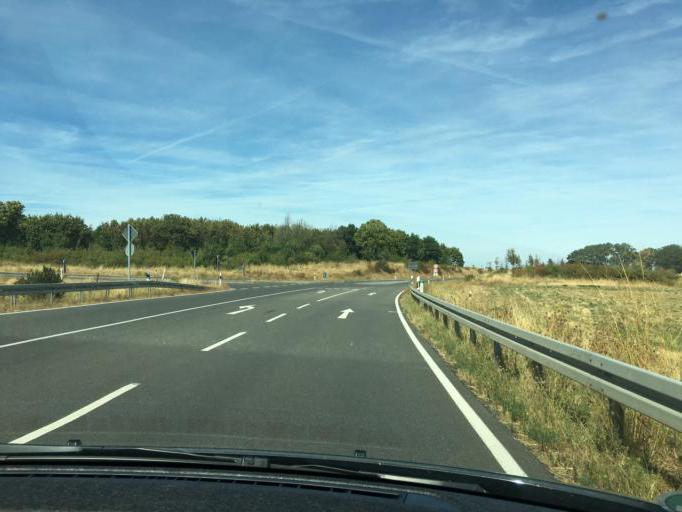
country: DE
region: North Rhine-Westphalia
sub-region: Regierungsbezirk Koln
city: Kreuzau
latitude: 50.7538
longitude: 6.4267
